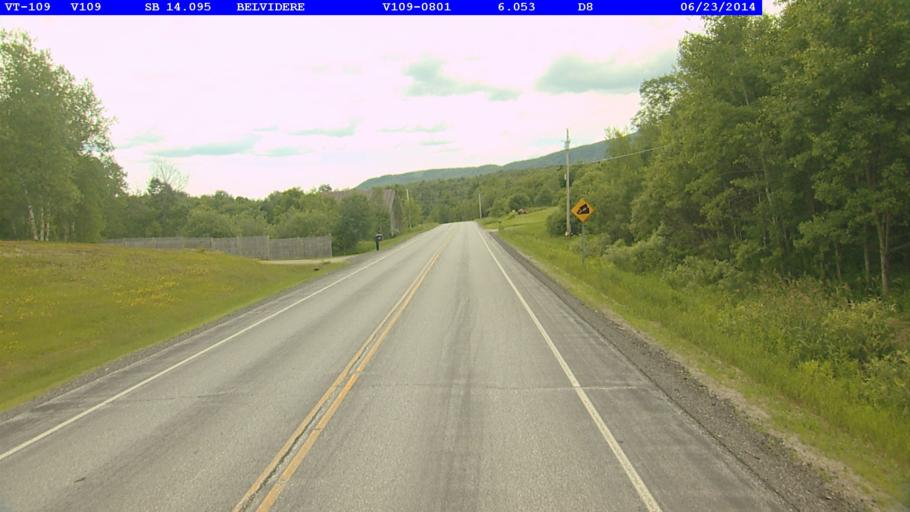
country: US
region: Vermont
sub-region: Lamoille County
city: Johnson
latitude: 44.7623
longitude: -72.6362
